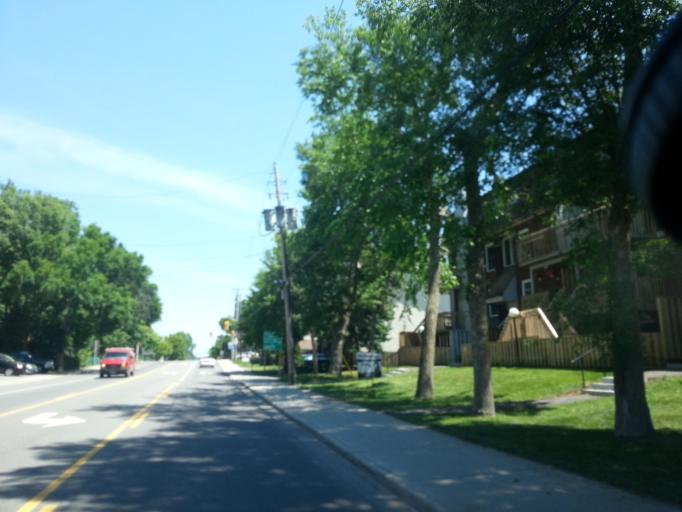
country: CA
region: Ontario
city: Carleton Place
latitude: 45.1427
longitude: -76.1516
